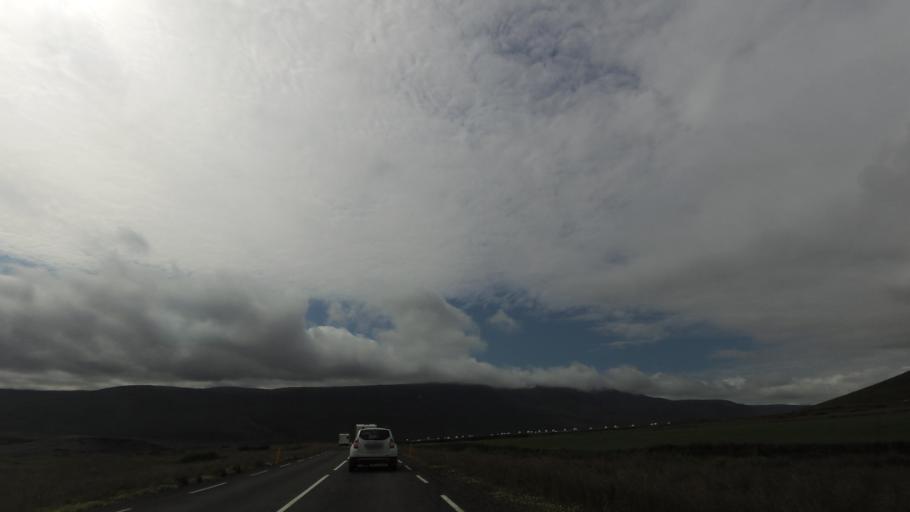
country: IS
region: Northeast
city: Laugar
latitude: 65.7098
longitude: -17.6132
